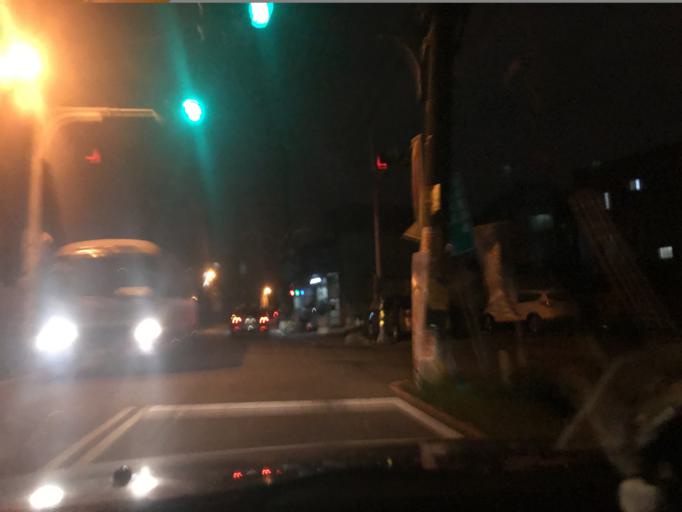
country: TW
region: Taiwan
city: Daxi
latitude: 24.9416
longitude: 121.2387
